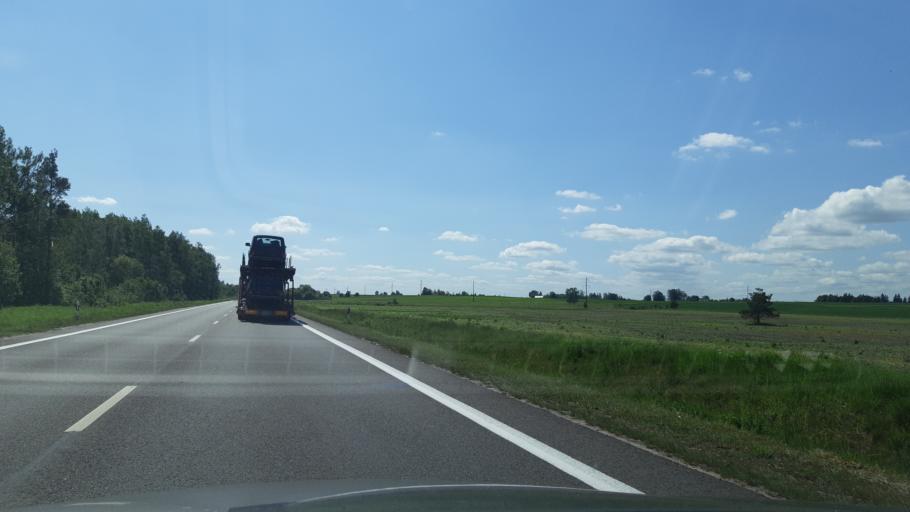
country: LT
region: Vilnius County
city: Ukmerge
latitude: 55.2321
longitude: 24.7144
